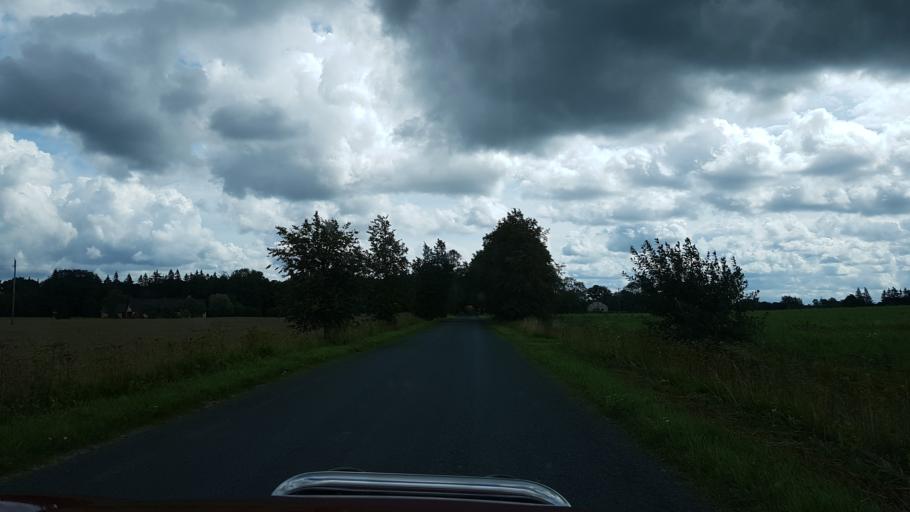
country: EE
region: Laeaene
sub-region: Lihula vald
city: Lihula
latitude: 58.7087
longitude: 24.0183
